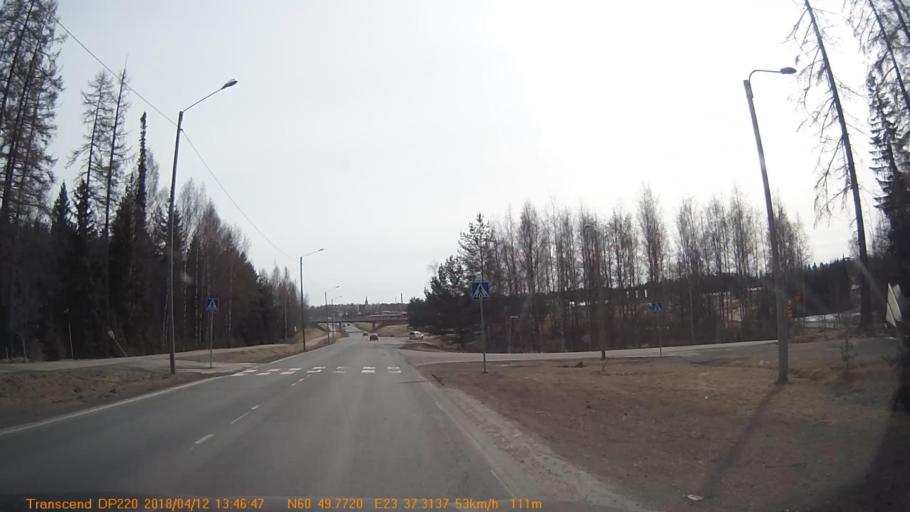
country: FI
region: Haeme
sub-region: Forssa
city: Forssa
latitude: 60.8295
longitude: 23.6219
